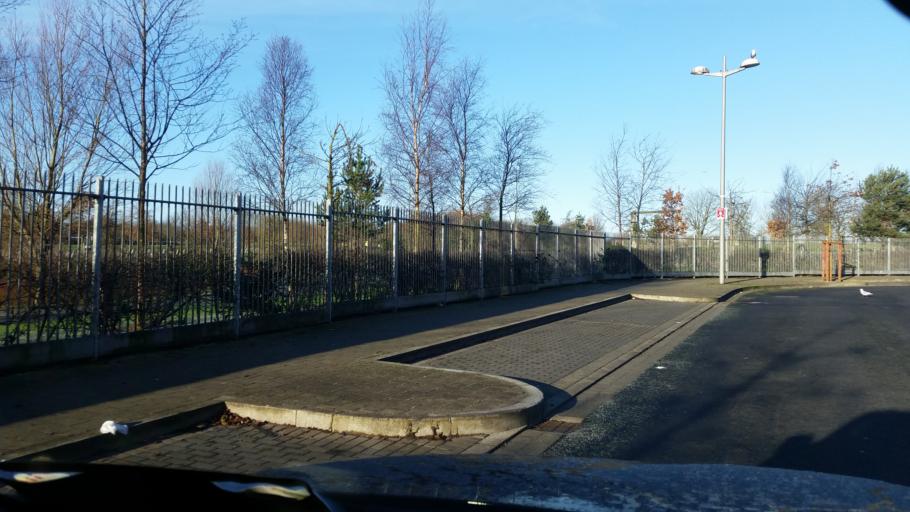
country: IE
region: Leinster
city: Ballymun
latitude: 53.3976
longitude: -6.2784
